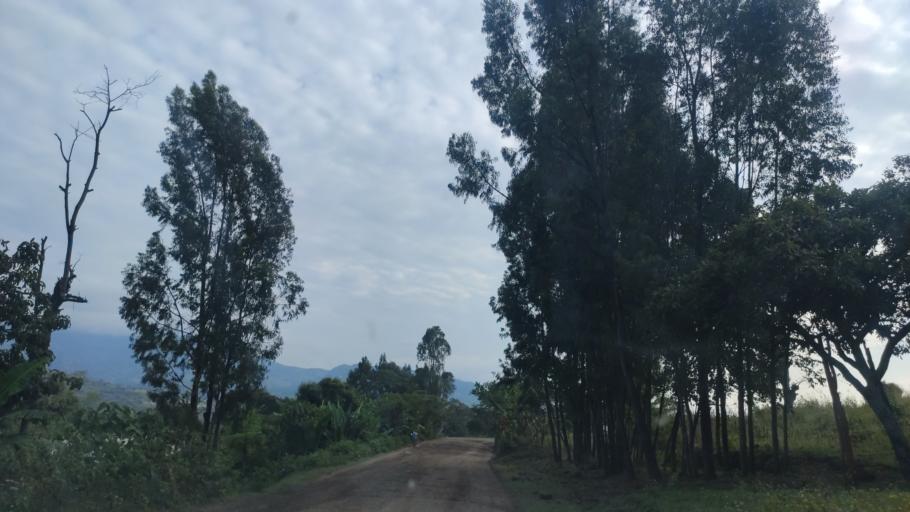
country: ET
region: Southern Nations, Nationalities, and People's Region
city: Arba Minch'
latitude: 6.4412
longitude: 37.3916
